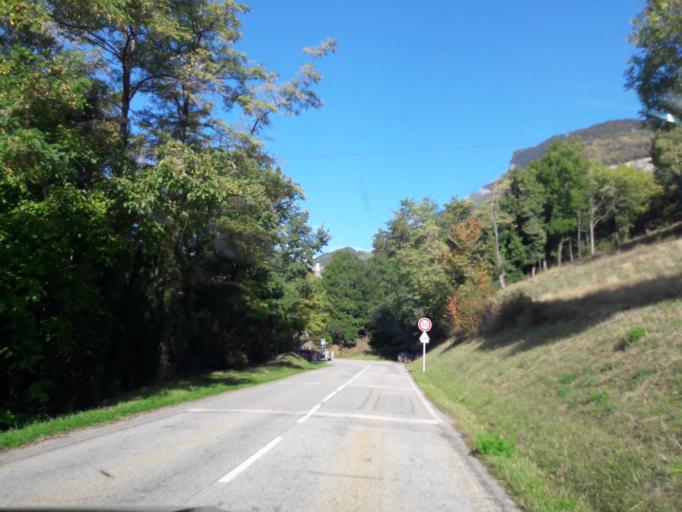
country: FR
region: Rhone-Alpes
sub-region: Departement de la Savoie
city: Saint-Jean-de-Maurienne
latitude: 45.3132
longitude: 6.3516
